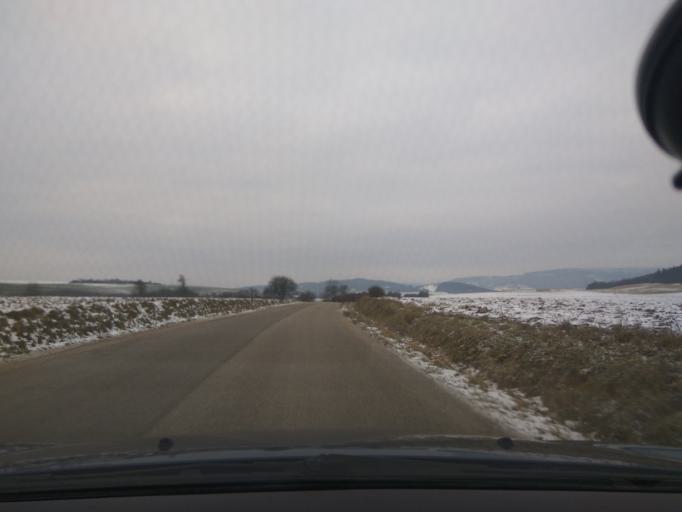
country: SK
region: Nitriansky
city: Stara Tura
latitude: 48.7926
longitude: 17.7276
